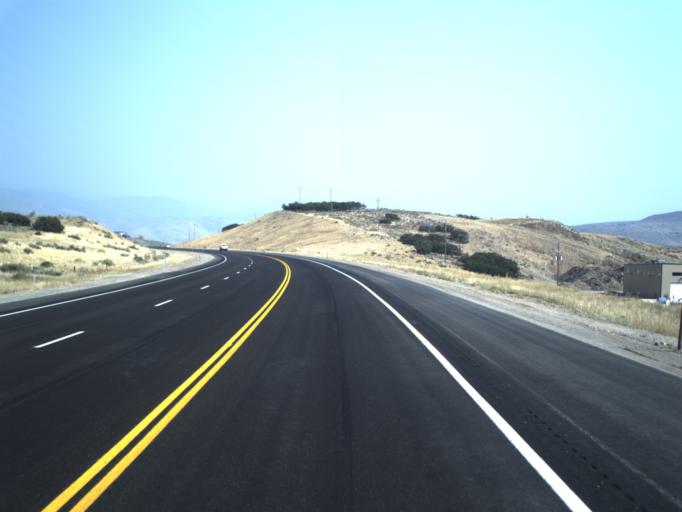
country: US
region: Utah
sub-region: Summit County
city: Kamas
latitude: 40.6341
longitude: -111.3524
